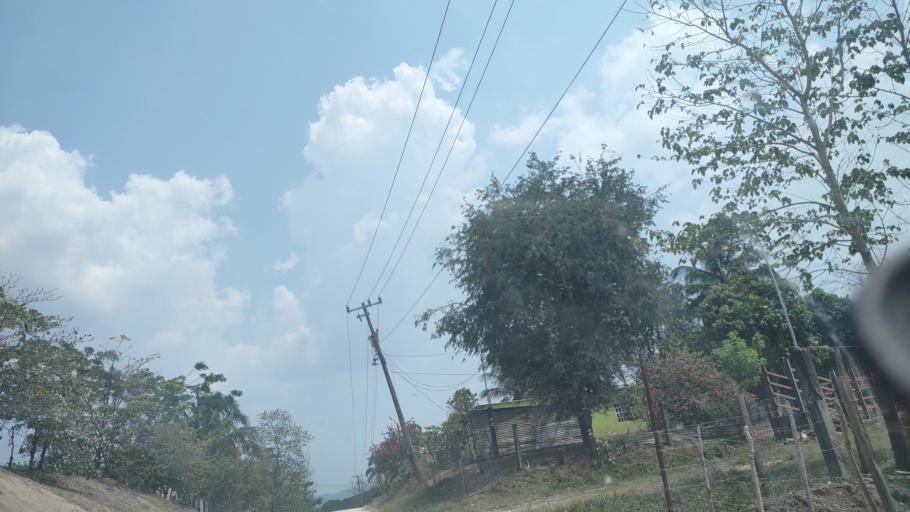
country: MX
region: Tabasco
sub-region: Huimanguillo
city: Francisco Rueda
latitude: 17.6036
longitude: -93.9055
